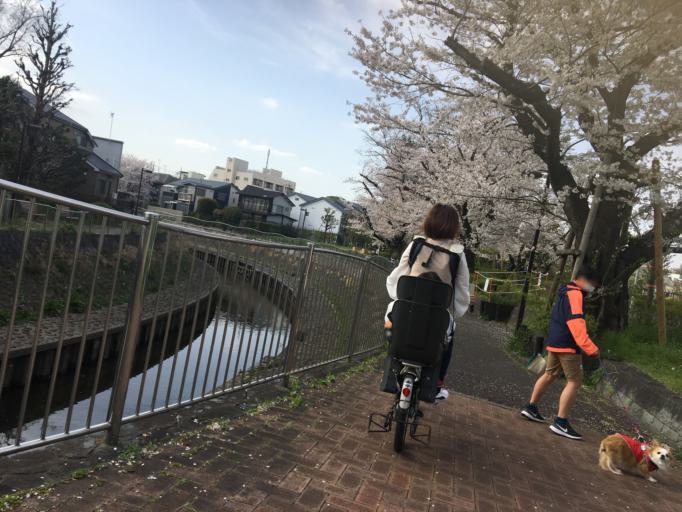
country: JP
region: Tokyo
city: Musashino
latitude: 35.6963
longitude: 139.6250
